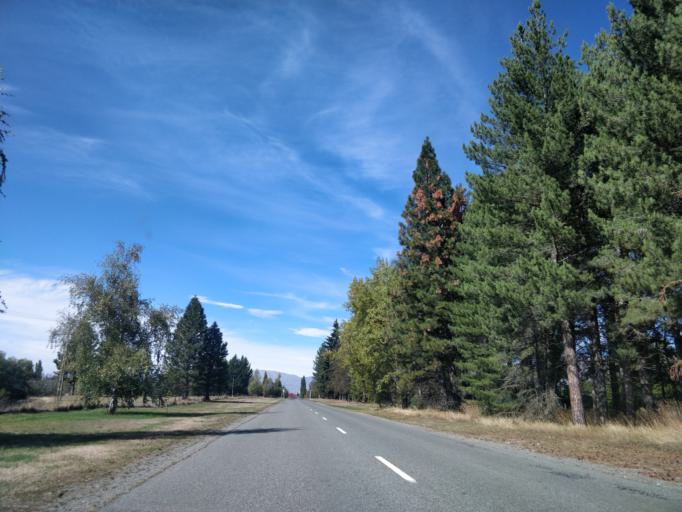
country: NZ
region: Canterbury
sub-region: Timaru District
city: Pleasant Point
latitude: -44.2505
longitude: 170.0991
